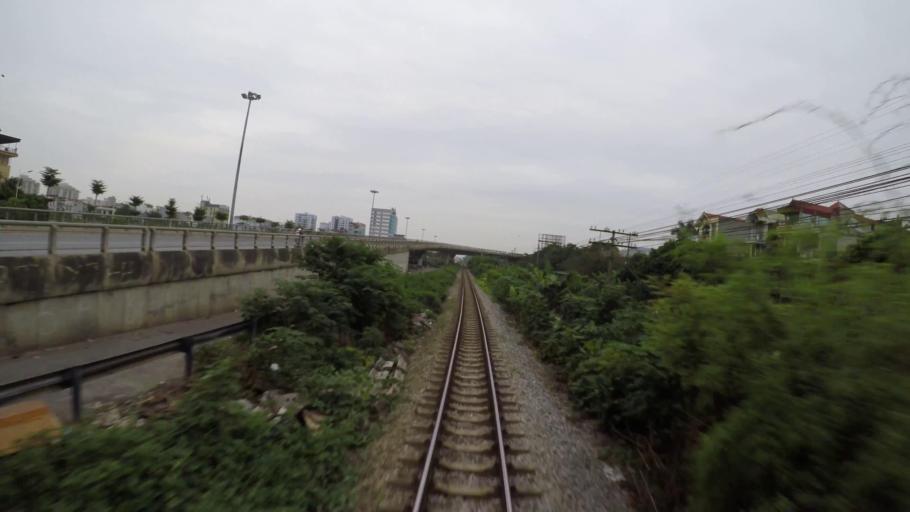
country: VN
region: Ha Noi
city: Trau Quy
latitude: 21.0077
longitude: 105.9566
